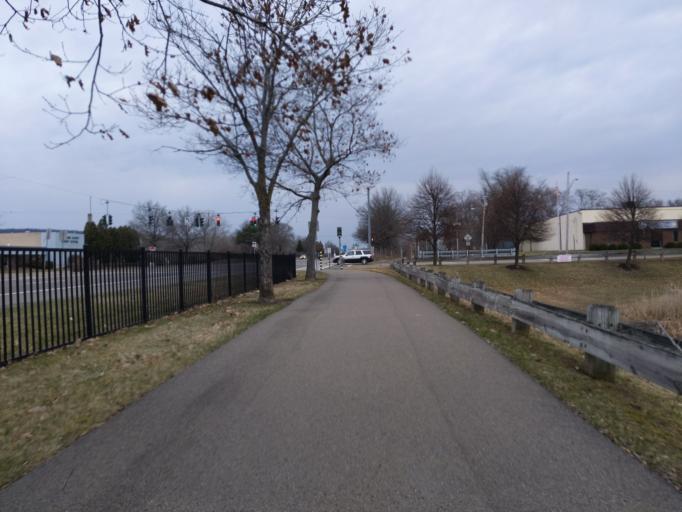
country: US
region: New York
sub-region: Chemung County
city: Elmira
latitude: 42.1058
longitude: -76.8108
